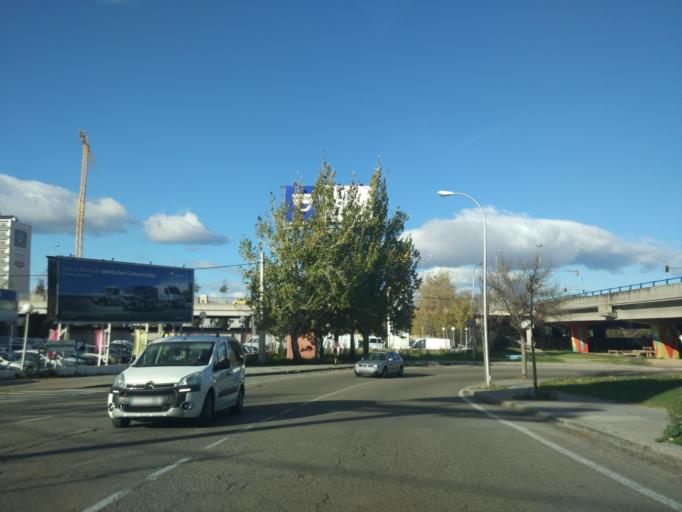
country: ES
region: Madrid
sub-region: Provincia de Madrid
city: Villaverde
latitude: 40.3446
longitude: -3.6933
